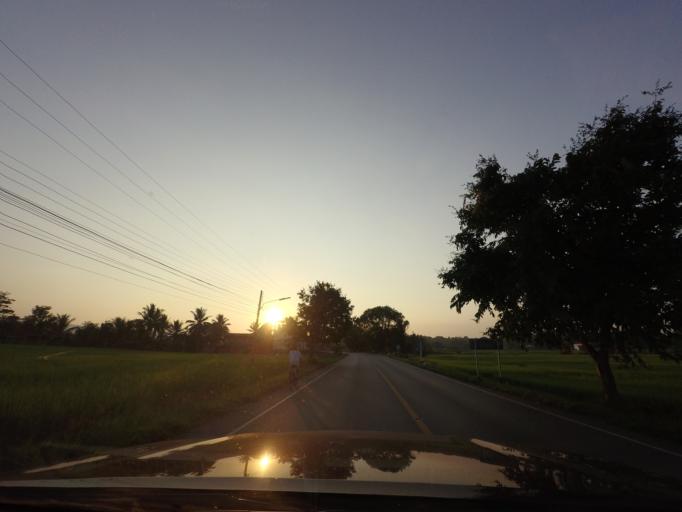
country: TH
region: Nan
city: Na Noi
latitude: 18.3262
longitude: 100.7224
